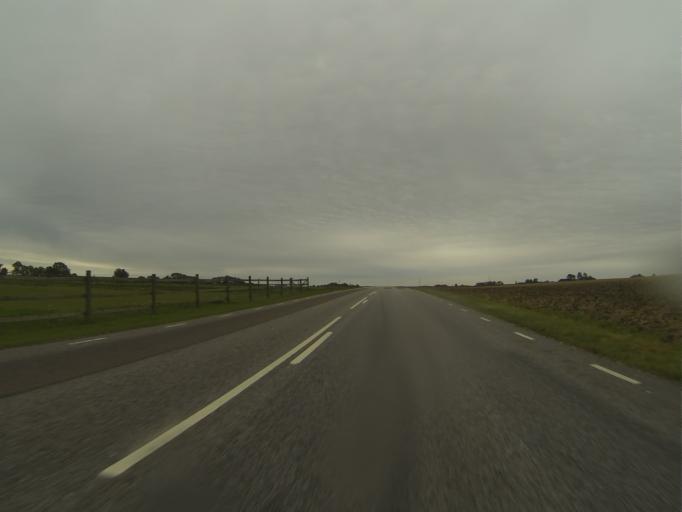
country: SE
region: Skane
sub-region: Svedala Kommun
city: Klagerup
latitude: 55.6318
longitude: 13.2909
